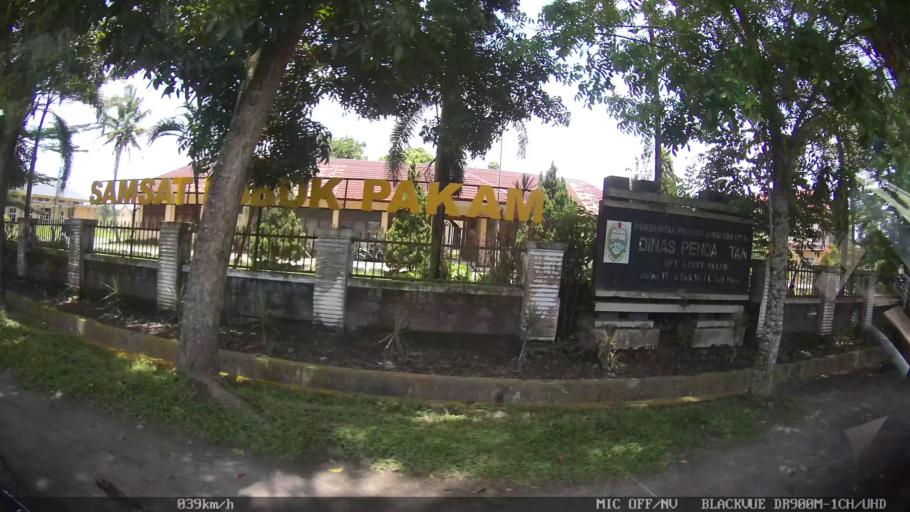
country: ID
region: North Sumatra
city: Percut
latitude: 3.5409
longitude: 98.8740
